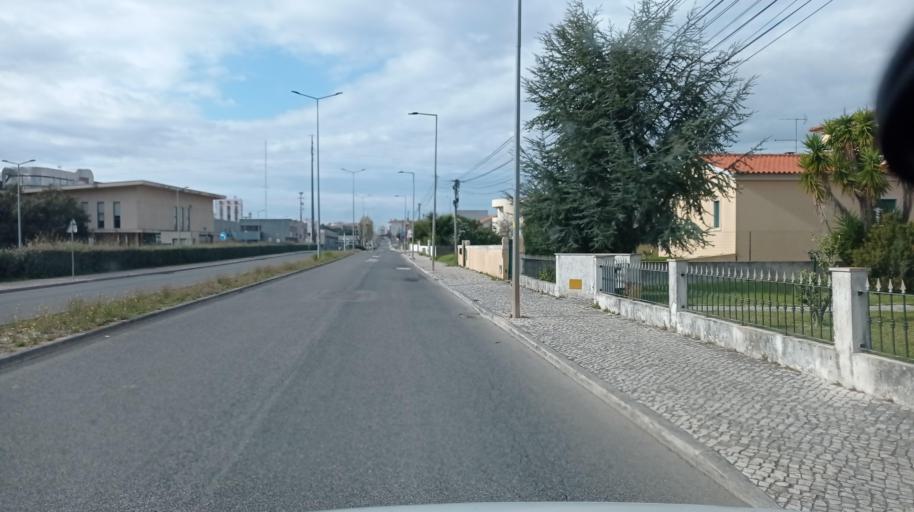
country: PT
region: Leiria
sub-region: Alcobaca
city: Benedita
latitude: 39.4248
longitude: -8.9688
